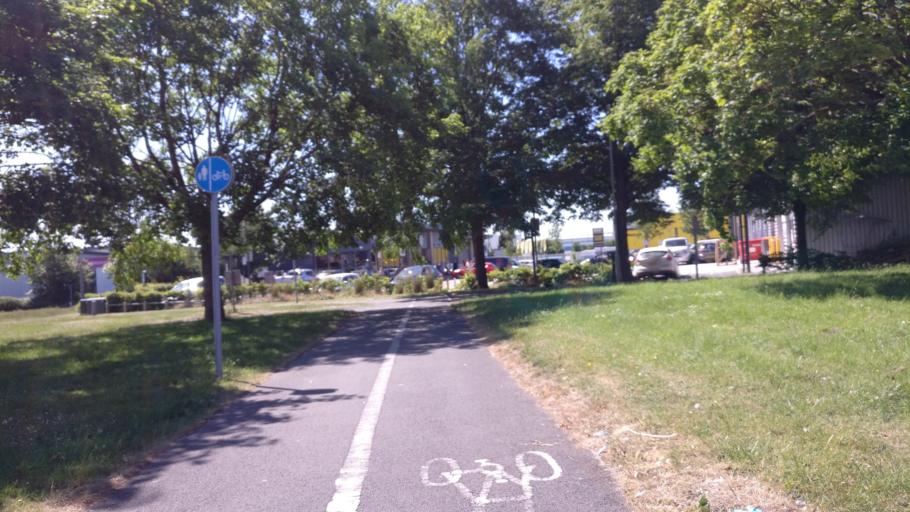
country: GB
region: England
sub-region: Hampshire
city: Basingstoke
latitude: 51.2743
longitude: -1.1057
